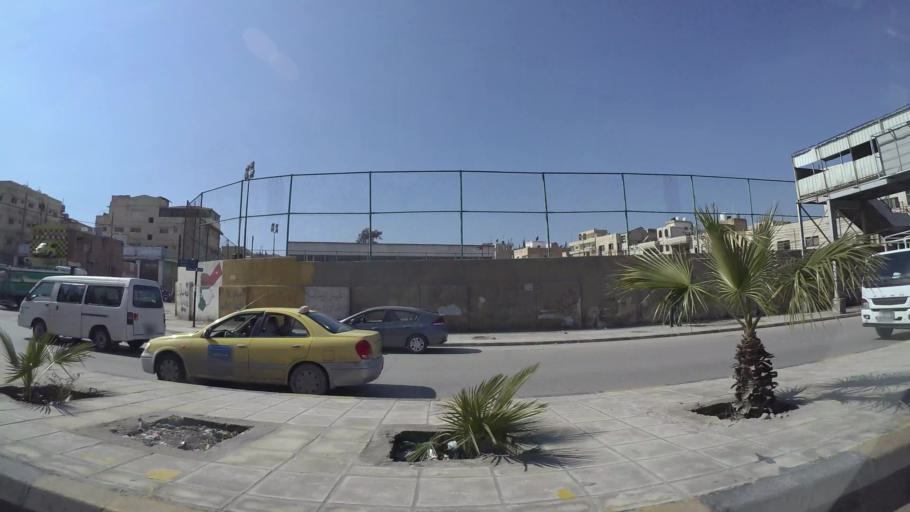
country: JO
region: Zarqa
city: Zarqa
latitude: 32.0682
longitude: 36.0969
